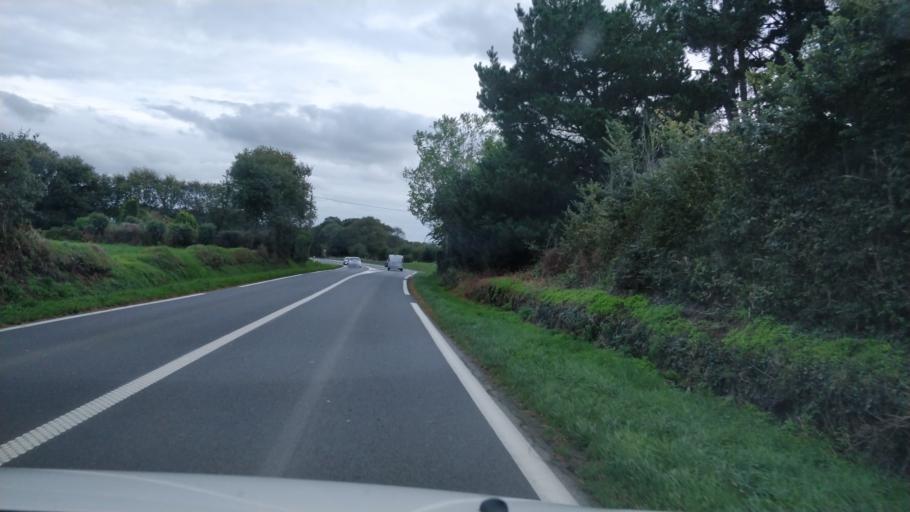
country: FR
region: Brittany
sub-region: Departement des Cotes-d'Armor
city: Lanvollon
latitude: 48.6503
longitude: -3.0106
